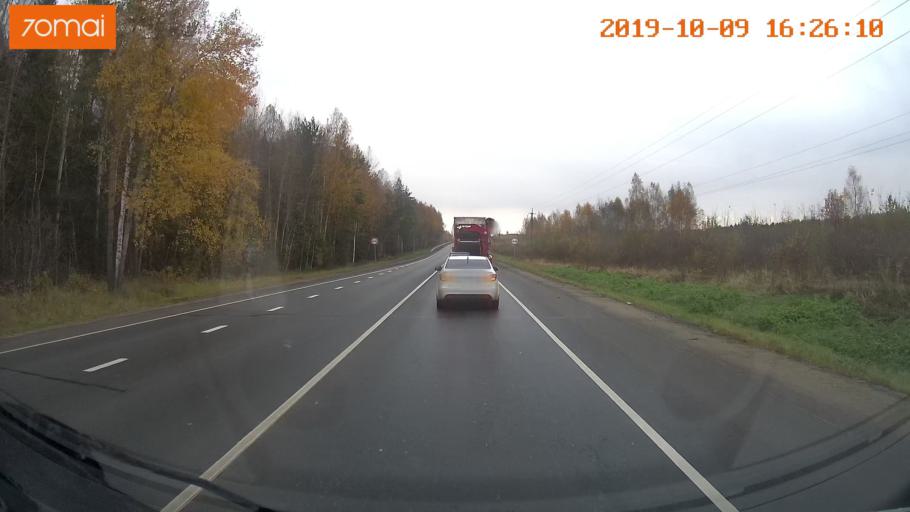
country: RU
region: Kostroma
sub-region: Kostromskoy Rayon
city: Kostroma
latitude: 57.6388
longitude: 40.9230
